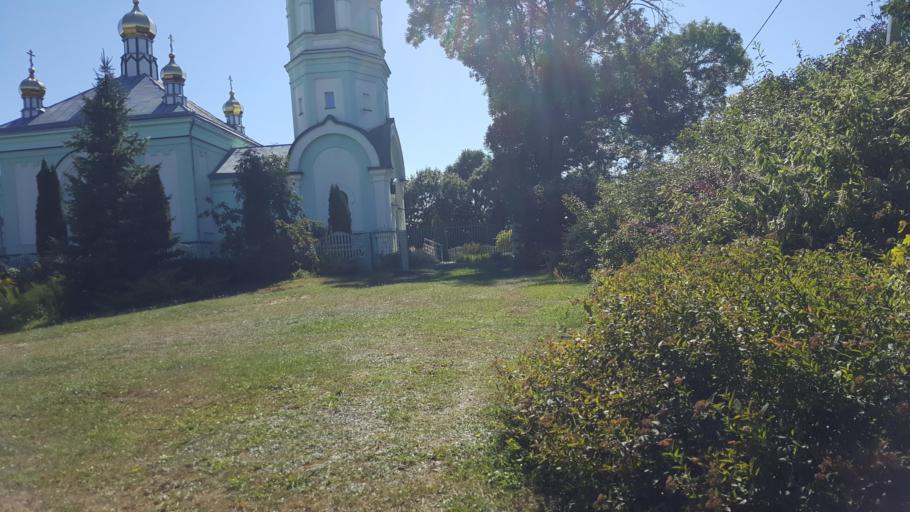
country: BY
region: Brest
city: Vysokaye
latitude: 52.2211
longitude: 23.4202
